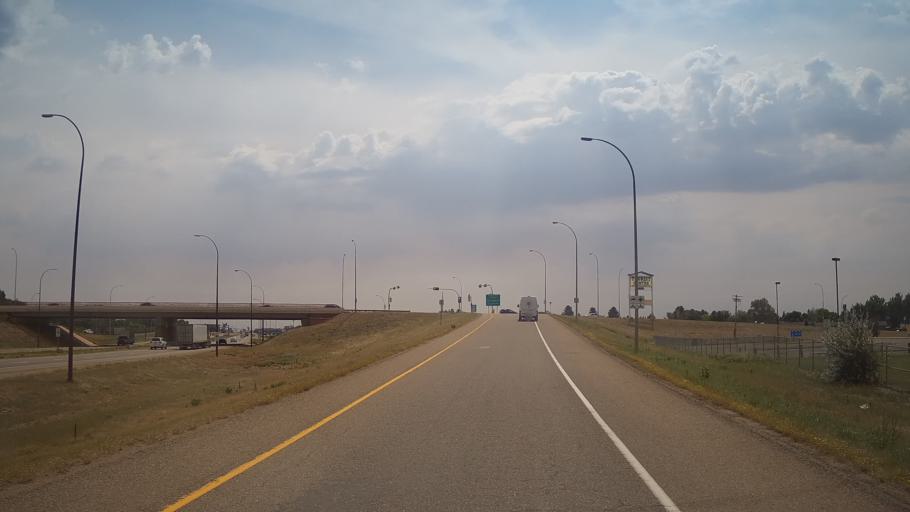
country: CA
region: Alberta
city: Medicine Hat
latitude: 50.0128
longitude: -110.6849
